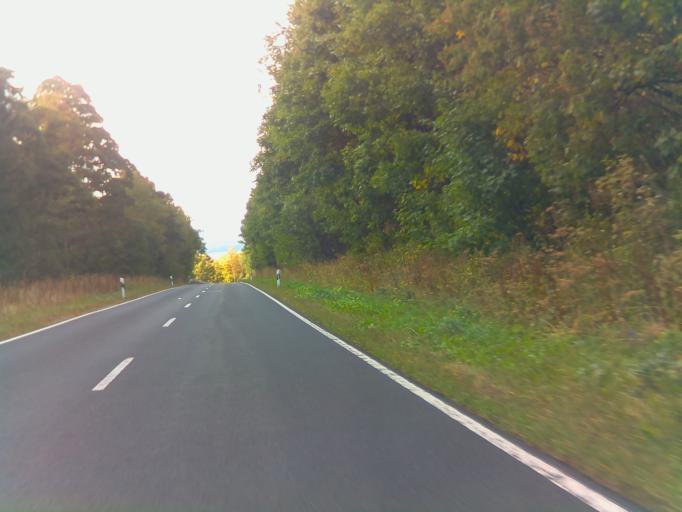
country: DE
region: Thuringia
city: Birx
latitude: 50.5109
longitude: 10.0397
